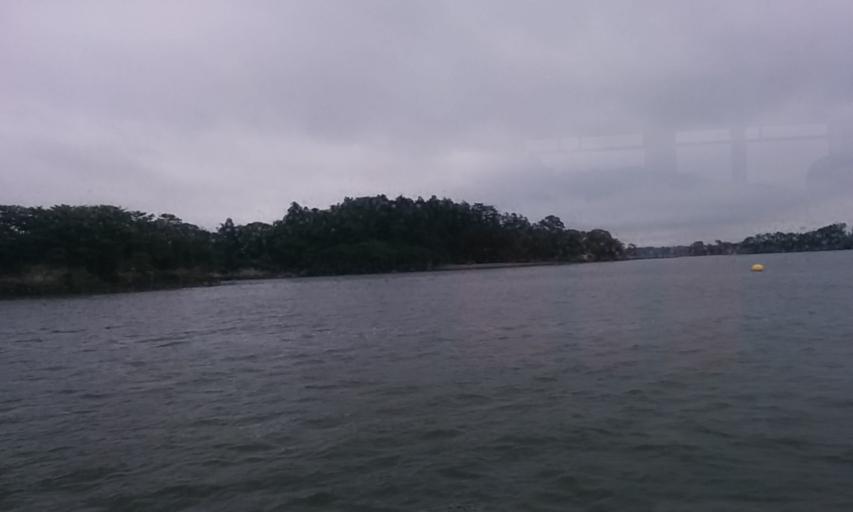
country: JP
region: Miyagi
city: Matsushima
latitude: 38.3636
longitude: 141.0673
